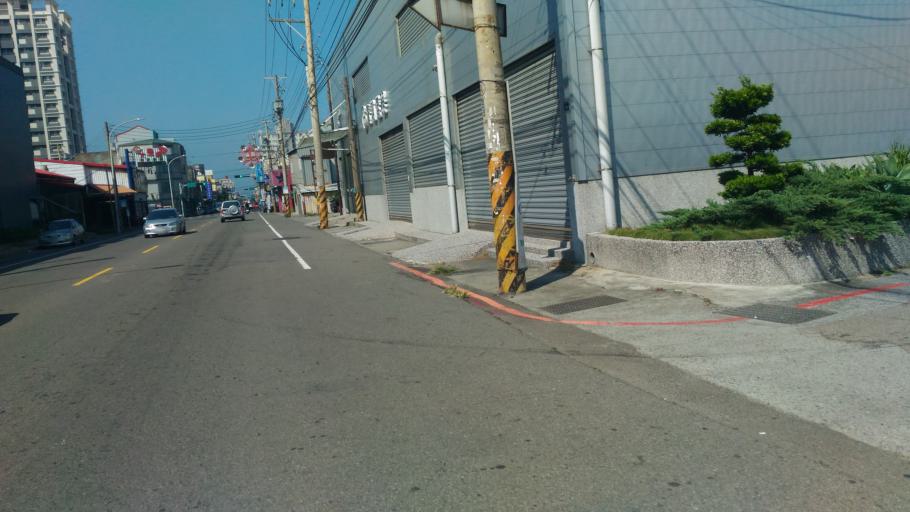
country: TW
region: Taiwan
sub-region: Hsinchu
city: Hsinchu
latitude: 24.8431
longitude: 120.9327
